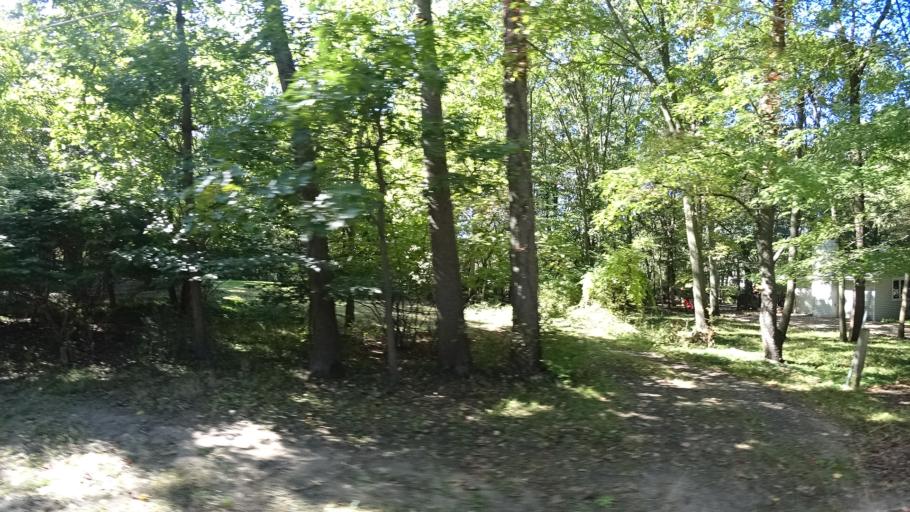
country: US
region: Indiana
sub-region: LaPorte County
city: Long Beach
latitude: 41.7525
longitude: -86.8210
